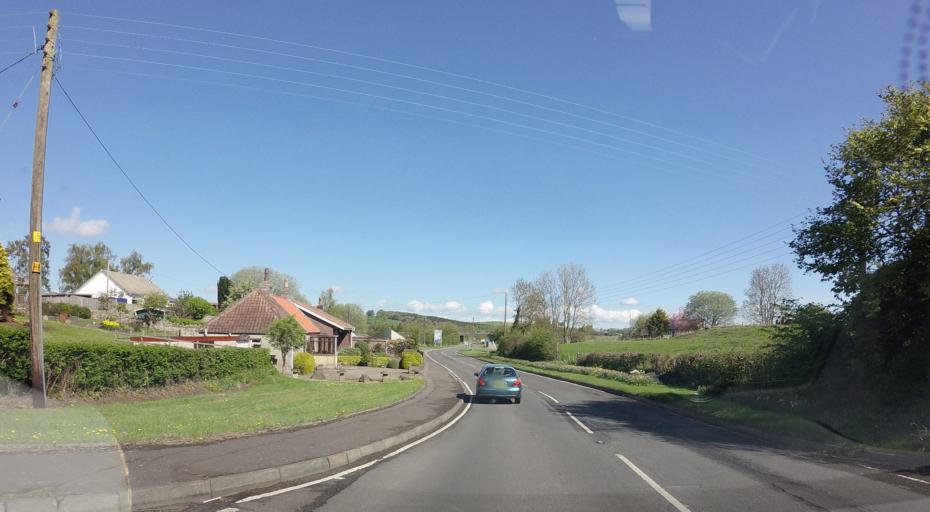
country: GB
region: Scotland
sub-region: West Lothian
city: Broxburn
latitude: 55.9784
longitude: -3.5084
